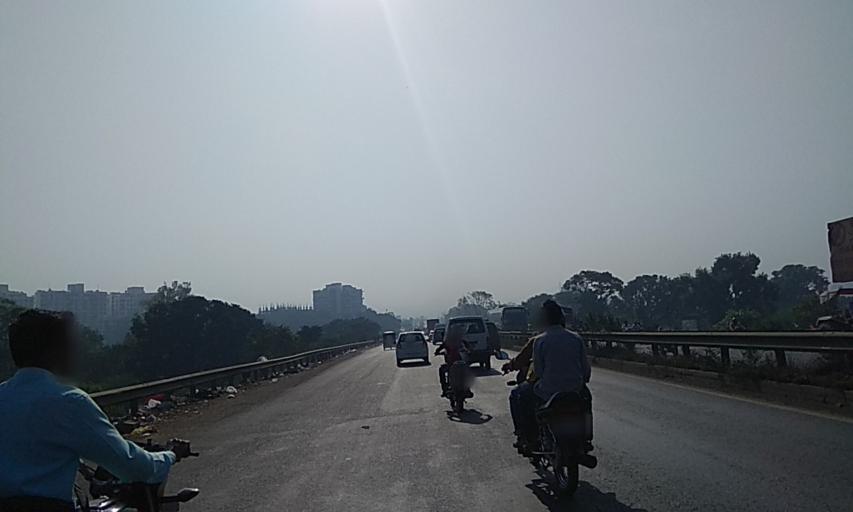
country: IN
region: Maharashtra
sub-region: Pune Division
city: Kharakvasla
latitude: 18.4770
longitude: 73.8073
